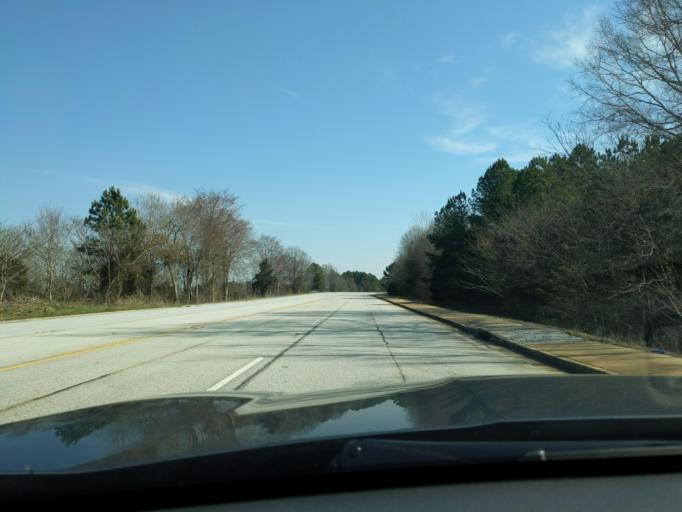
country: US
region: South Carolina
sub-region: Abbeville County
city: Calhoun Falls
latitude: 34.0963
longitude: -82.5840
